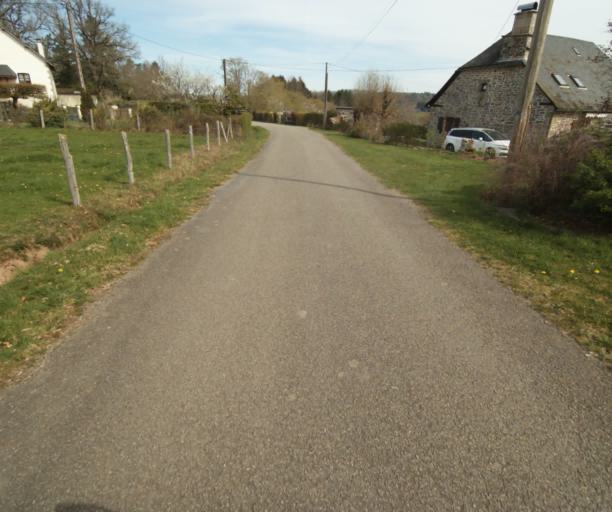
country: FR
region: Limousin
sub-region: Departement de la Correze
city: Correze
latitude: 45.3699
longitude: 1.8200
